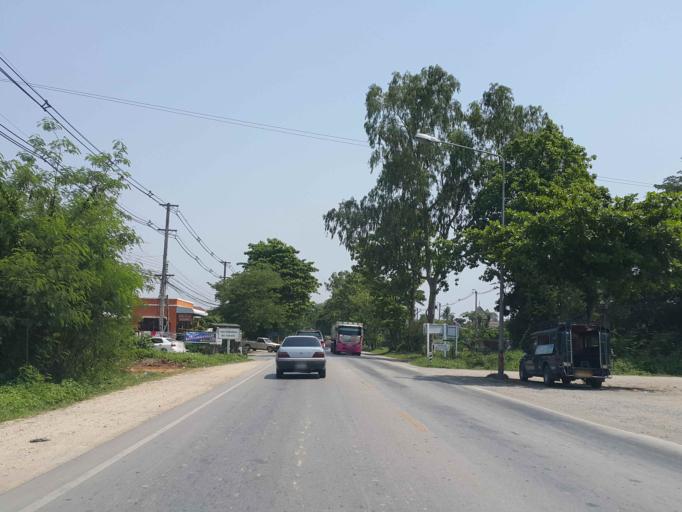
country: TH
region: Chiang Mai
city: San Sai
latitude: 18.9544
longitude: 98.9840
